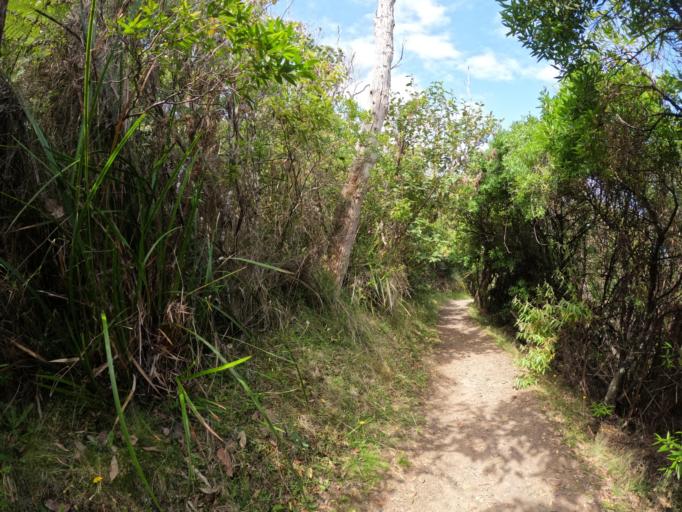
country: AU
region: Victoria
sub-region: Colac-Otway
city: Apollo Bay
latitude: -38.7915
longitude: 143.6224
